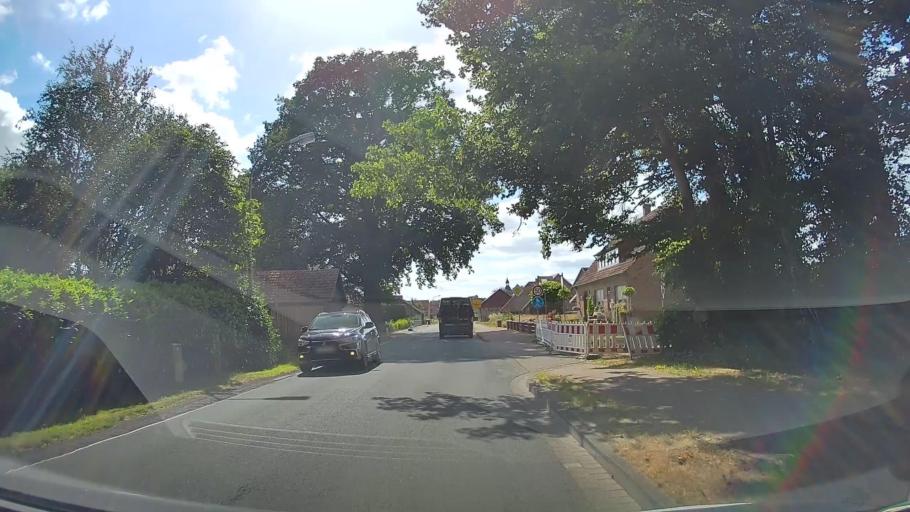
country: DE
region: Lower Saxony
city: Alfhausen
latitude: 52.5003
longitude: 7.9612
